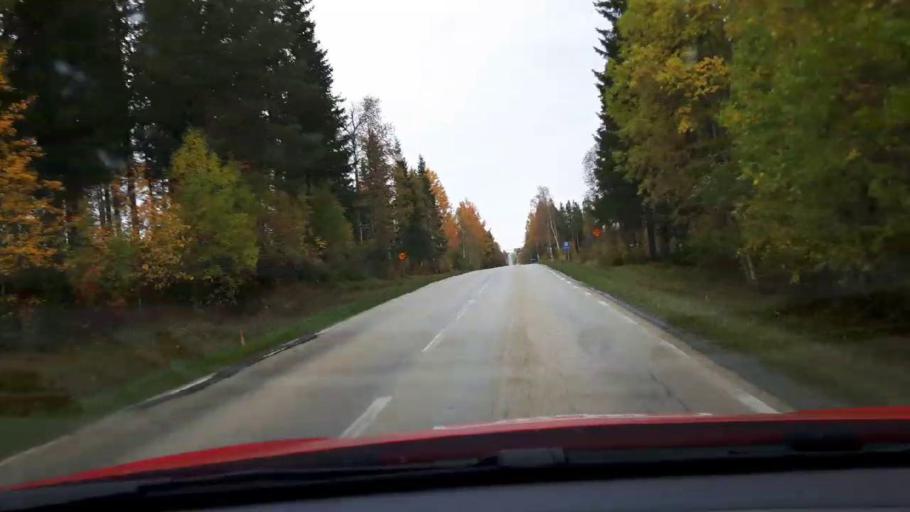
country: SE
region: Jaemtland
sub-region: Bergs Kommun
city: Hoverberg
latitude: 62.9920
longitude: 14.3393
